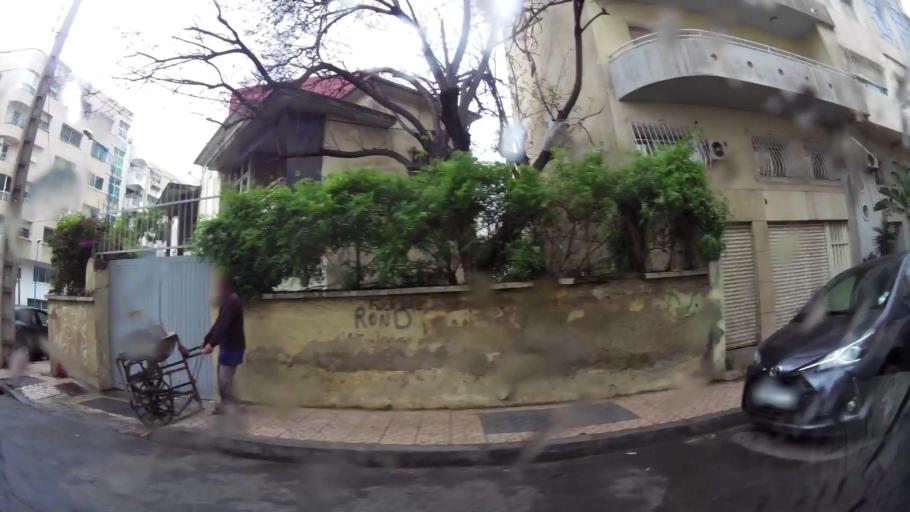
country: MA
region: Grand Casablanca
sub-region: Casablanca
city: Casablanca
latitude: 33.5722
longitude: -7.6113
